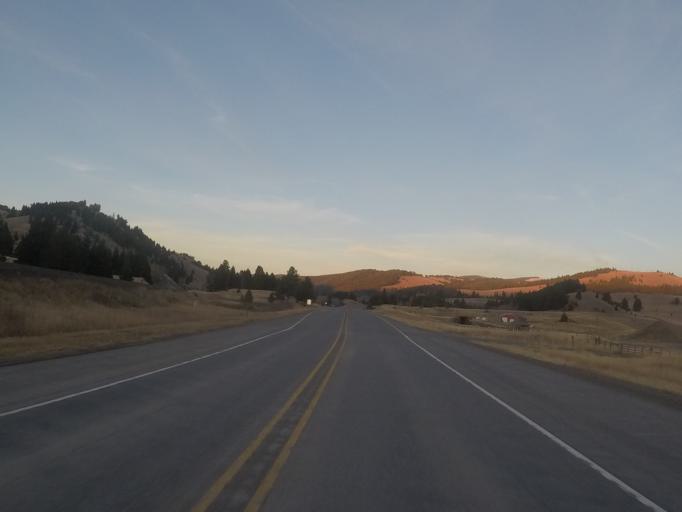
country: US
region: Montana
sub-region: Lewis and Clark County
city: Helena West Side
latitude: 46.5572
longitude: -112.3936
